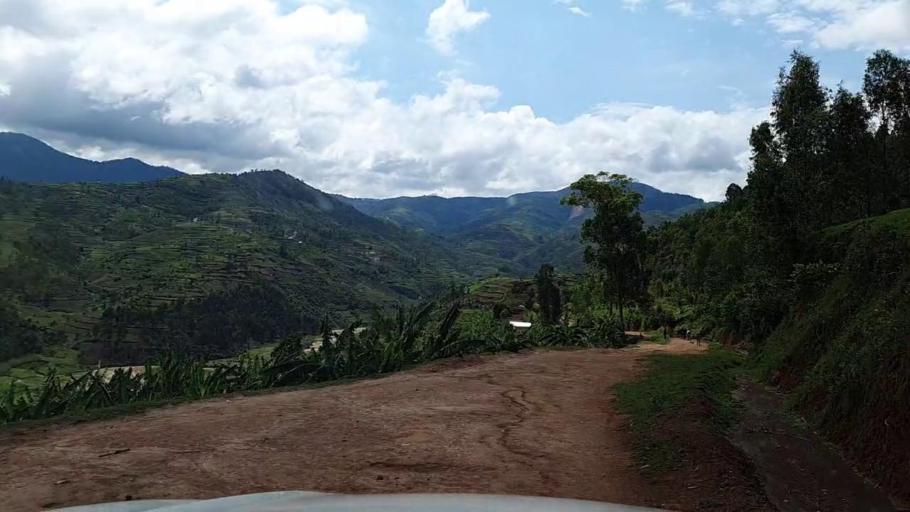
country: RW
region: Southern Province
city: Gikongoro
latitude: -2.3604
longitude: 29.5493
